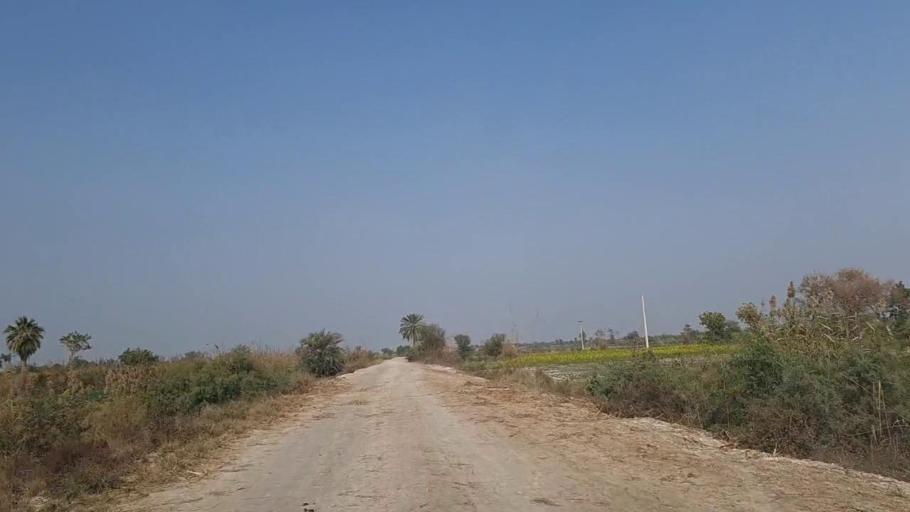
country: PK
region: Sindh
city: Daur
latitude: 26.4833
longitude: 68.4513
